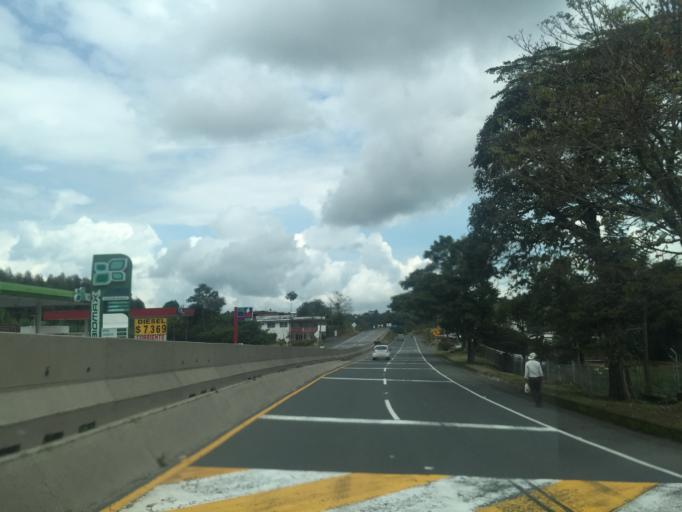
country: CO
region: Risaralda
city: Santa Rosa de Cabal
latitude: 4.8964
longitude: -75.6277
